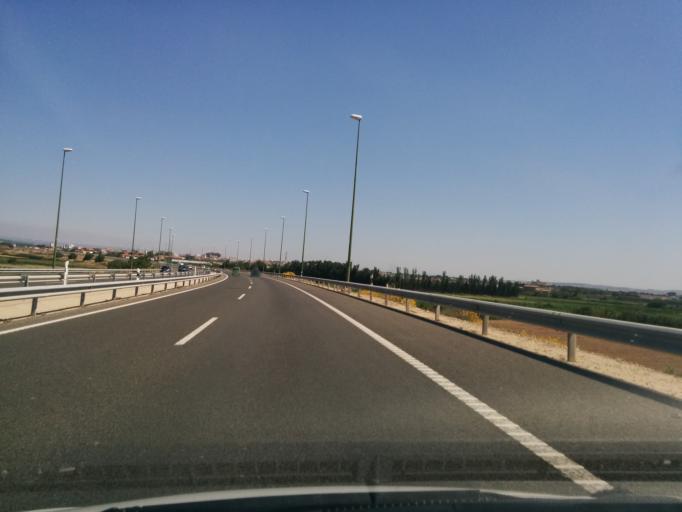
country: ES
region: Aragon
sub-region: Provincia de Zaragoza
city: Zaragoza
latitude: 41.6395
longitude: -0.8313
